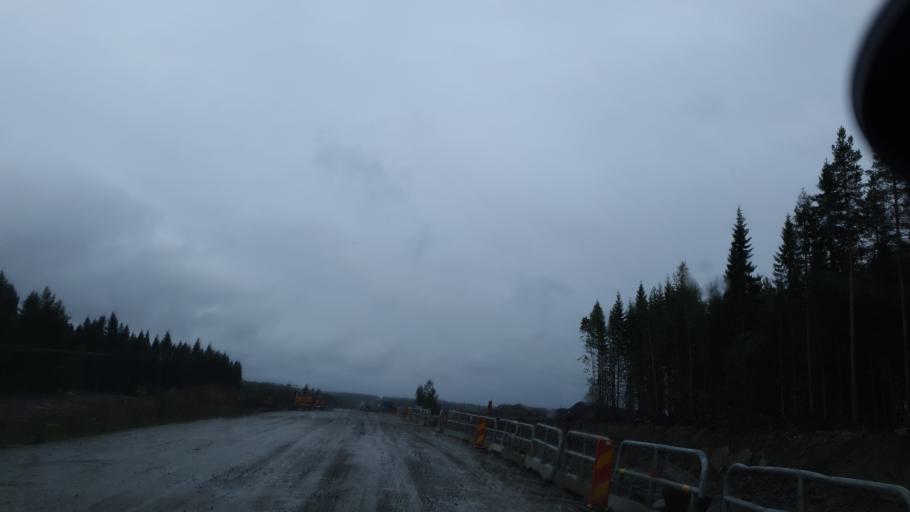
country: SE
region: Vaesterbotten
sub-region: Skelleftea Kommun
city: Soedra Bergsbyn
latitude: 64.7412
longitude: 21.0739
